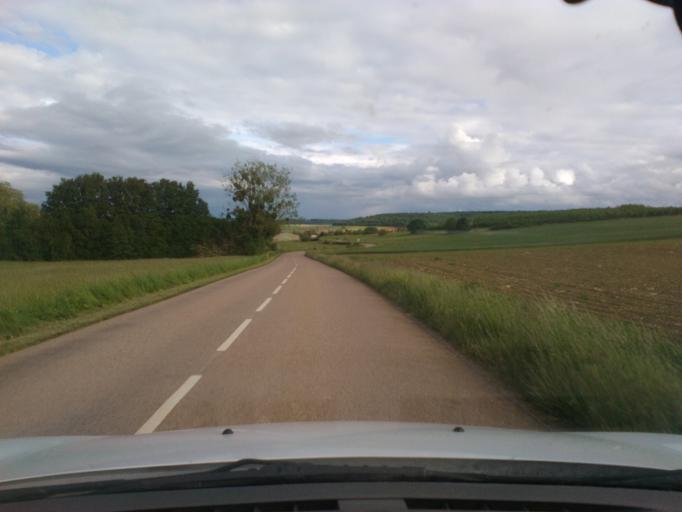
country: FR
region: Lorraine
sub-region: Departement des Vosges
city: Mirecourt
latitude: 48.3231
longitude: 6.0443
